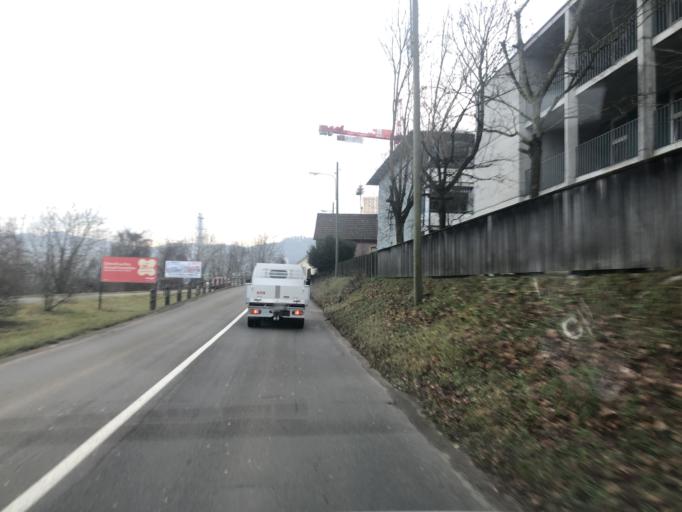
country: CH
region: Aargau
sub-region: Bezirk Baden
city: Turgi
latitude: 47.4876
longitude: 8.2631
